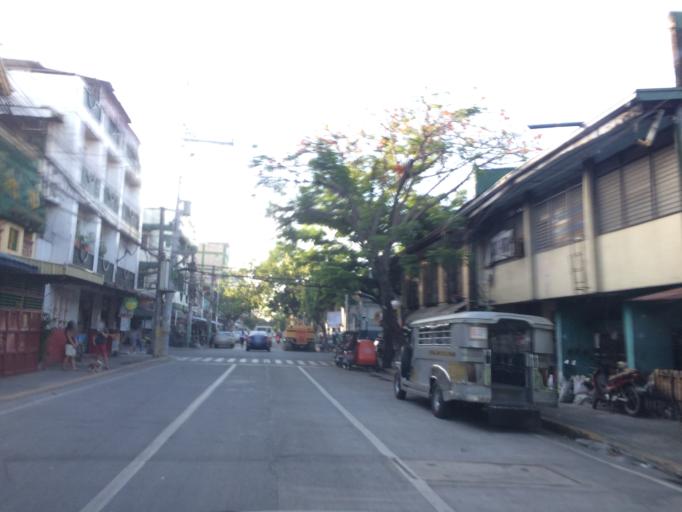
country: PH
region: Metro Manila
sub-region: City of Manila
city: Manila
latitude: 14.6164
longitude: 120.9906
